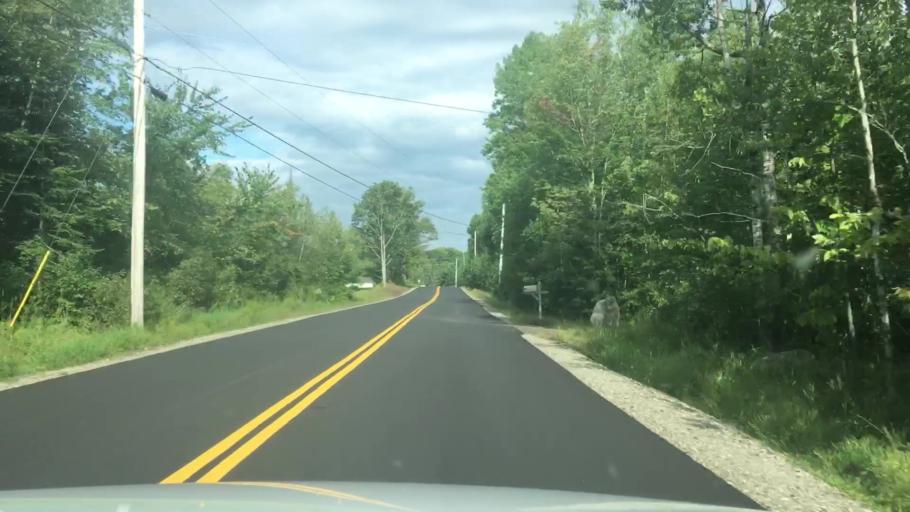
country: US
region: Maine
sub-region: Androscoggin County
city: Lisbon
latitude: 44.0573
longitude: -70.0830
